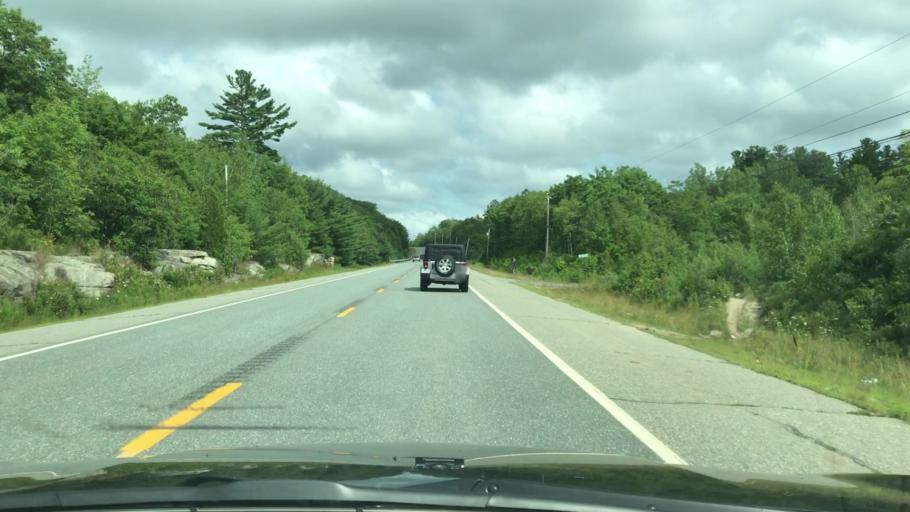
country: US
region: Maine
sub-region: Hancock County
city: Surry
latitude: 44.5655
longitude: -68.6084
